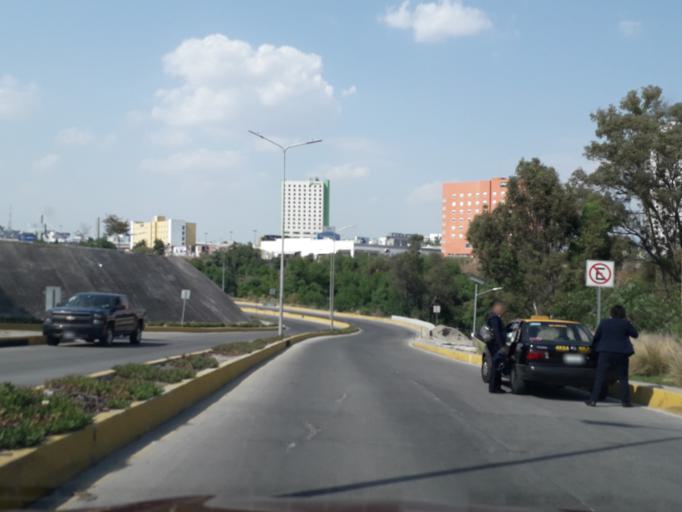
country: MX
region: Puebla
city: Puebla
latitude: 19.0307
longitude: -98.2262
